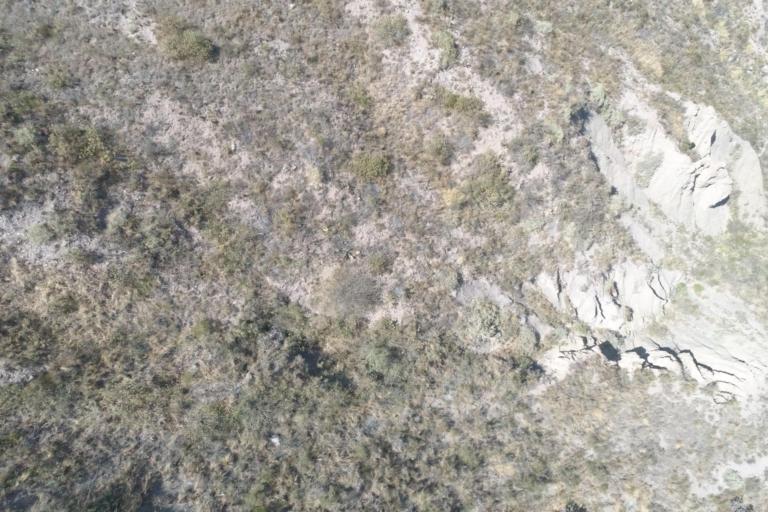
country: BO
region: La Paz
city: La Paz
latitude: -16.6220
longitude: -68.0398
